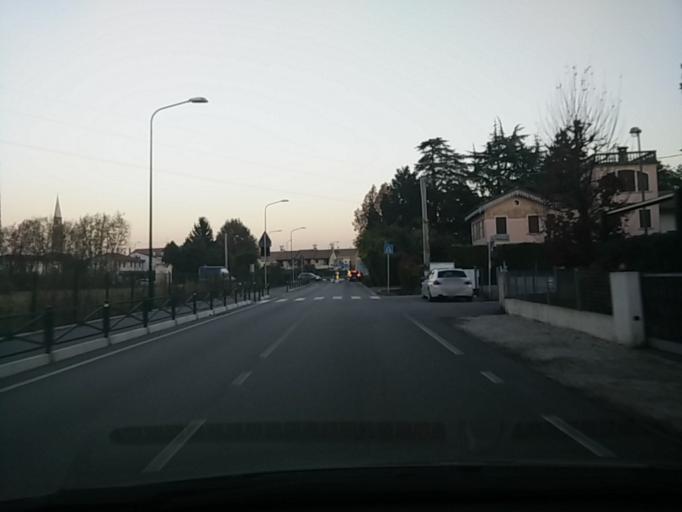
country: IT
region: Veneto
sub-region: Provincia di Treviso
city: Lancenigo-Villorba
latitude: 45.7099
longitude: 12.2688
